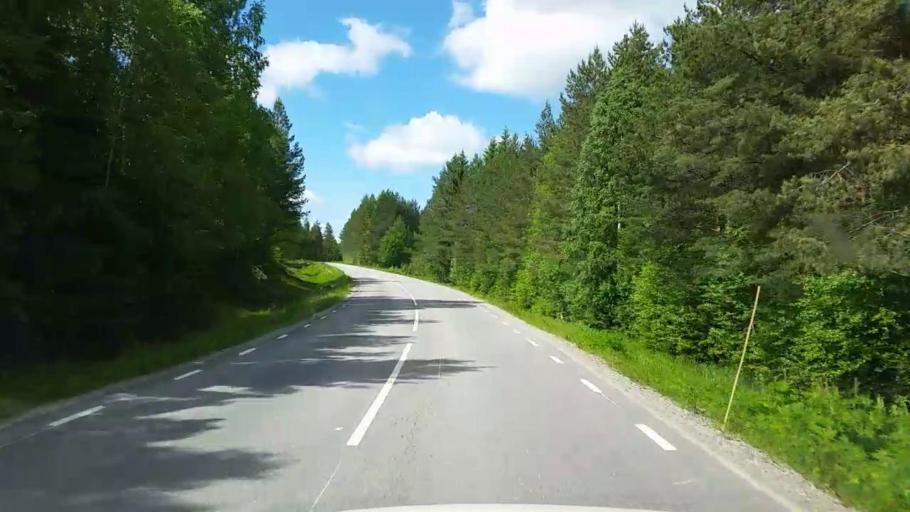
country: SE
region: Gaevleborg
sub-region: Ovanakers Kommun
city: Alfta
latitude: 61.2736
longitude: 16.1144
